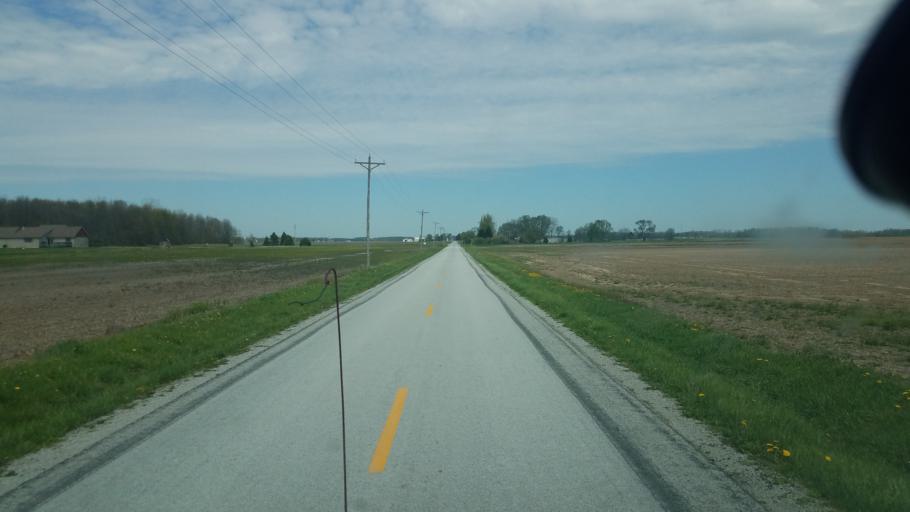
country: US
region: Ohio
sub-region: Hardin County
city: Kenton
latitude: 40.6497
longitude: -83.7248
